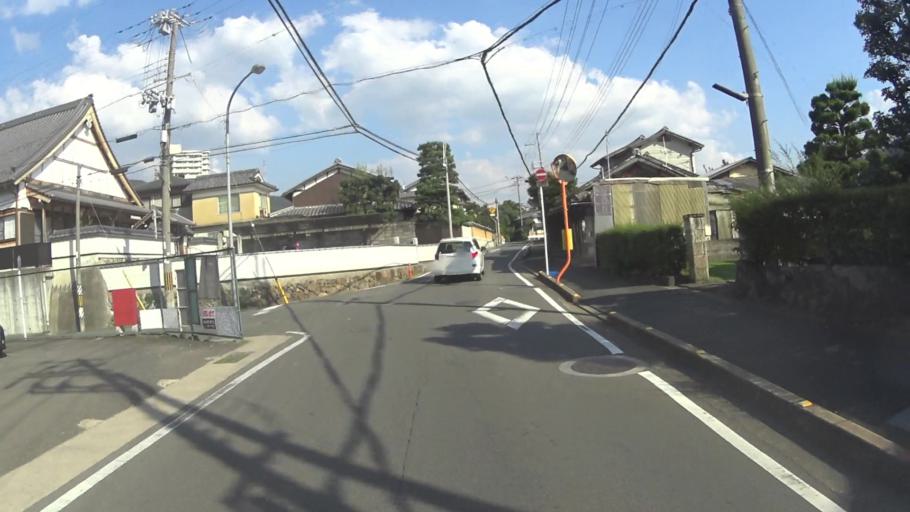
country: JP
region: Kyoto
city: Kameoka
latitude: 35.0095
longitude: 135.6005
